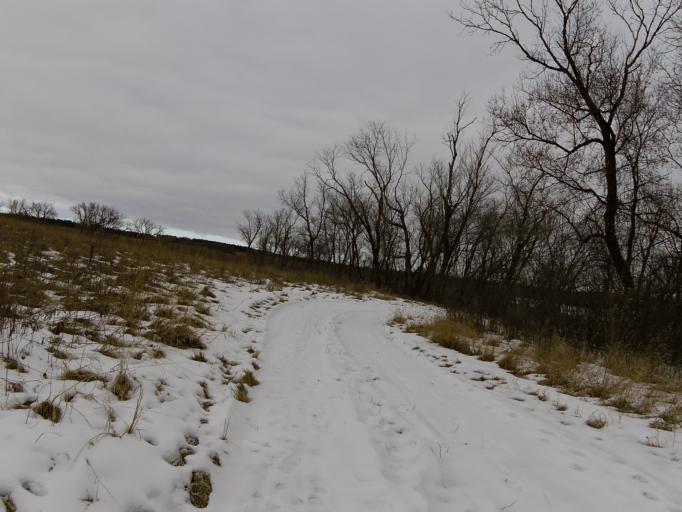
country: US
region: Wisconsin
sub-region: Pierce County
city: Prescott
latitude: 44.7975
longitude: -92.8220
